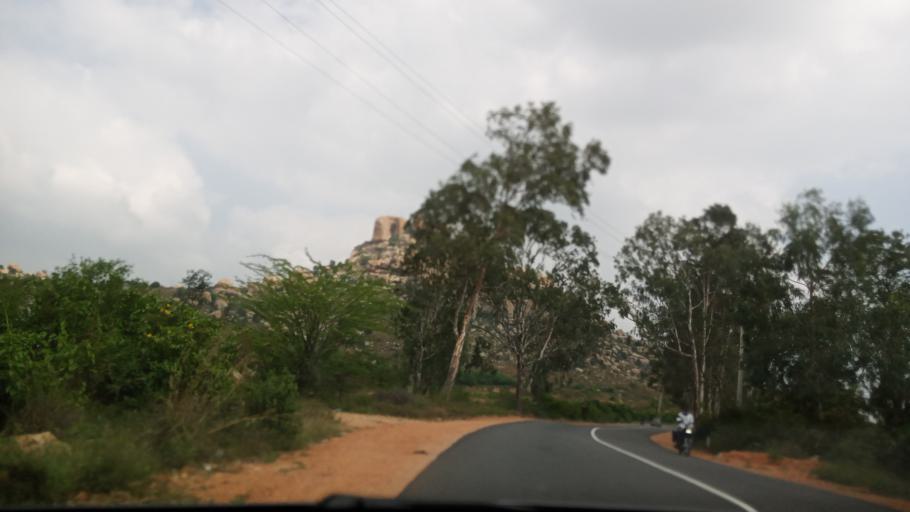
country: IN
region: Andhra Pradesh
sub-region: Chittoor
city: Madanapalle
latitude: 13.6359
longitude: 78.6126
